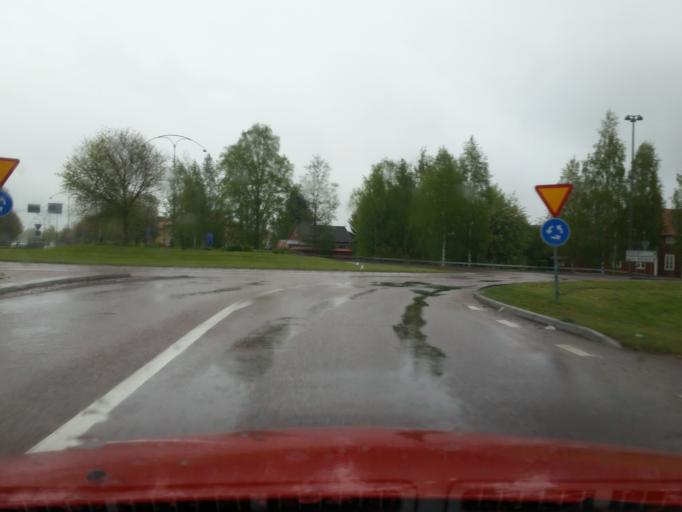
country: SE
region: Dalarna
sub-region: Borlange Kommun
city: Borlaenge
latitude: 60.4775
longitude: 15.4359
